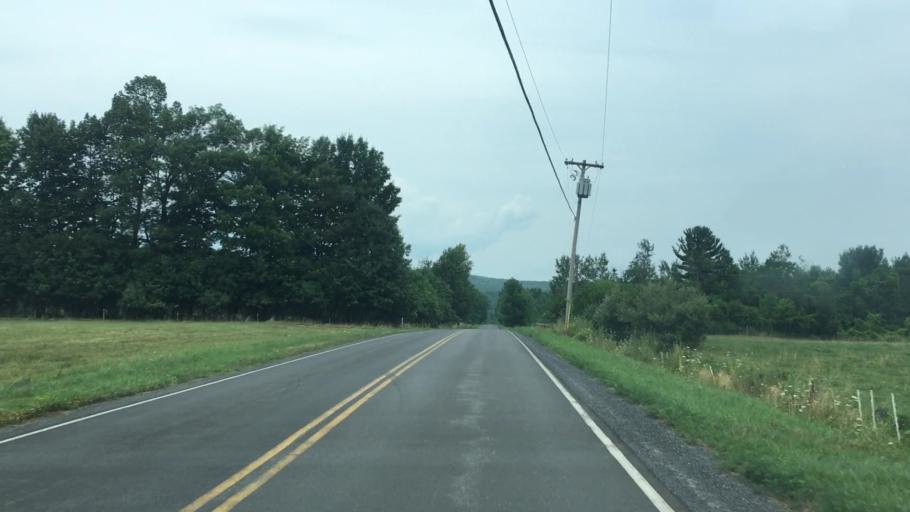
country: US
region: New York
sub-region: Clinton County
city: Peru
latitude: 44.6010
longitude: -73.6283
